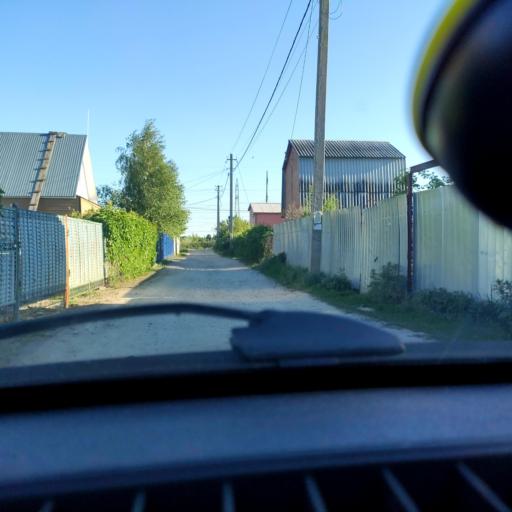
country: RU
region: Samara
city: Tol'yatti
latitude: 53.5908
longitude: 49.3147
